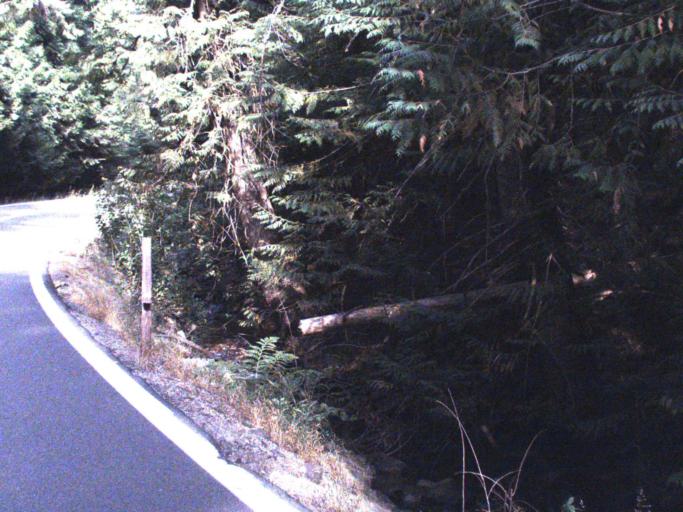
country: US
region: Washington
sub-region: Spokane County
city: Otis Orchards-East Farms
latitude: 47.8757
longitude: -117.1509
